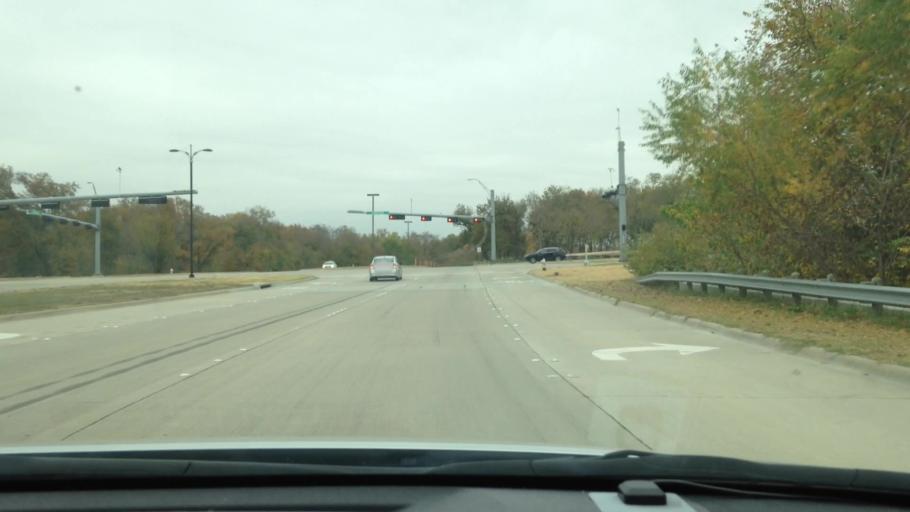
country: US
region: Texas
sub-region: Collin County
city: Allen
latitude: 33.1242
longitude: -96.7191
